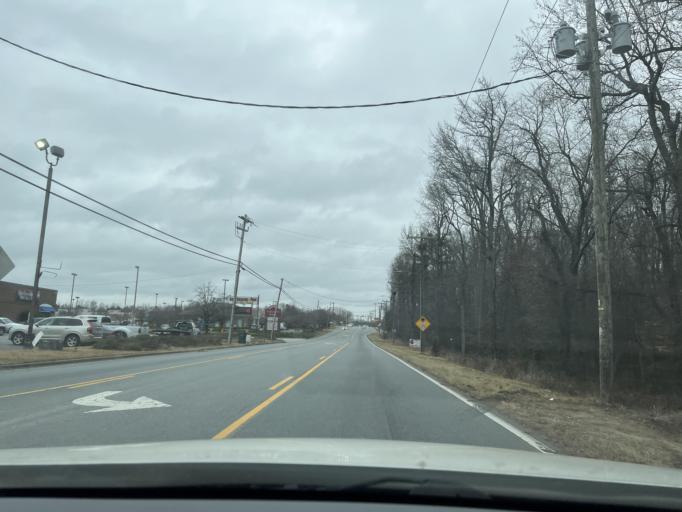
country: US
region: North Carolina
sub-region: Guilford County
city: Pleasant Garden
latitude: 36.0058
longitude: -79.8060
